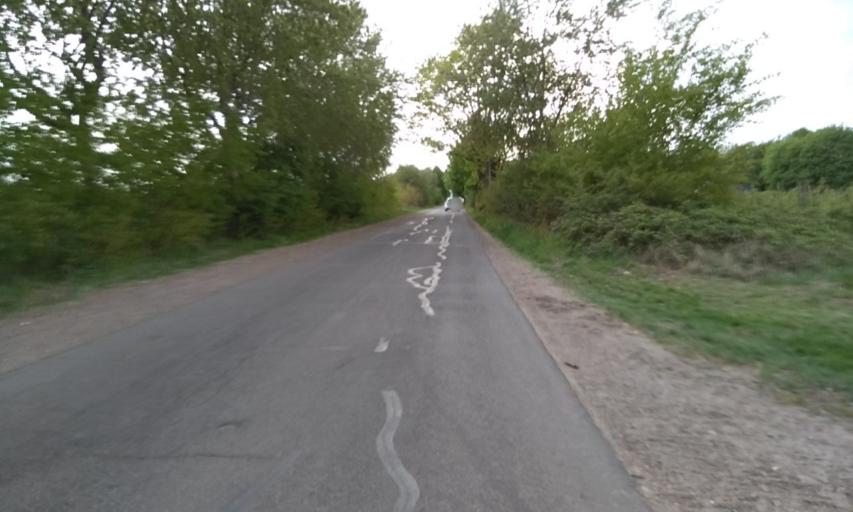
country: DE
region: Lower Saxony
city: Bliedersdorf
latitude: 53.4826
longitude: 9.5811
